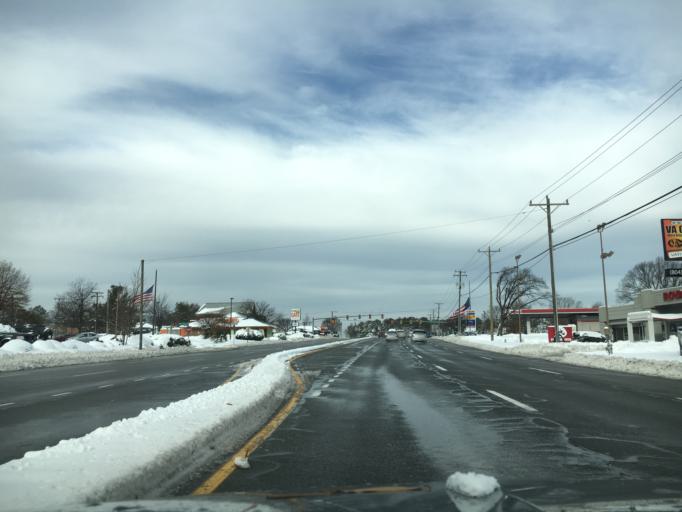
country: US
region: Virginia
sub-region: Henrico County
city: Laurel
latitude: 37.6285
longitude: -77.5339
